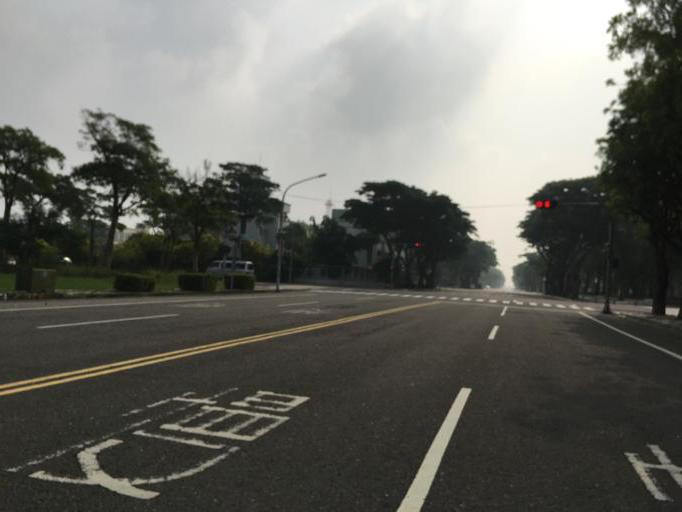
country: TW
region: Taiwan
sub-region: Chiayi
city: Taibao
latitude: 23.4581
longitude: 120.2880
